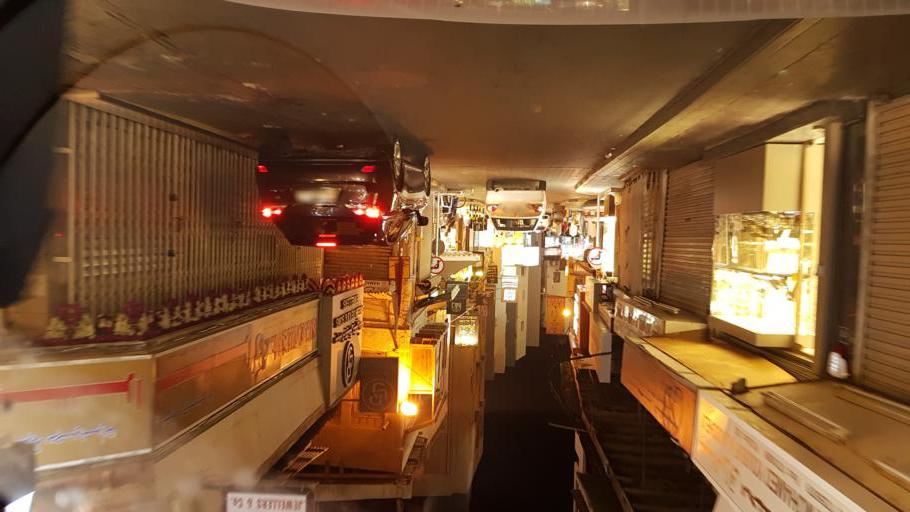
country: BH
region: Manama
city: Manama
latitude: 26.2316
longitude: 50.5768
